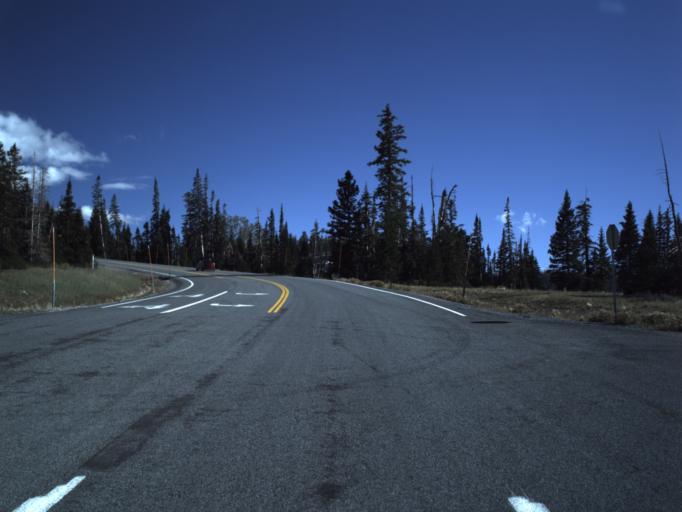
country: US
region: Utah
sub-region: Iron County
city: Parowan
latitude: 37.6789
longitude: -112.8482
